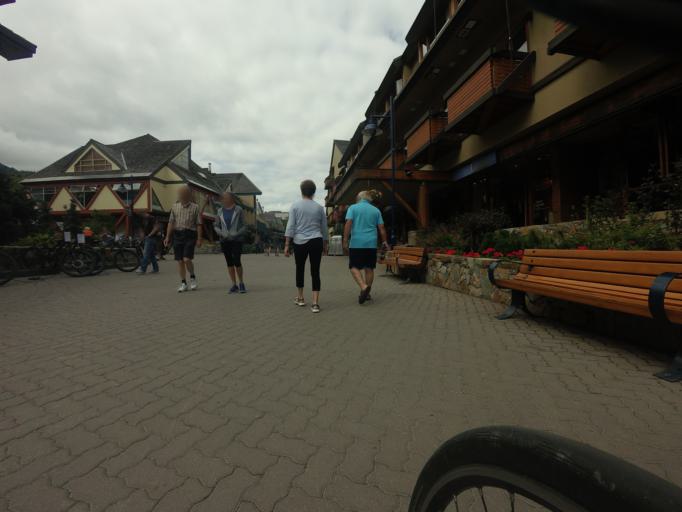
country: CA
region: British Columbia
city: Whistler
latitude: 50.1151
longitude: -122.9551
